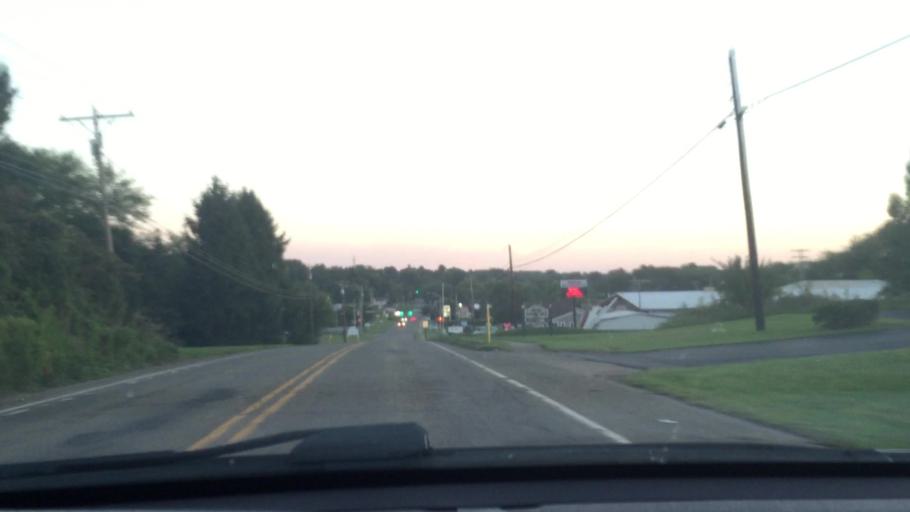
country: US
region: Pennsylvania
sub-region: Butler County
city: Slippery Rock
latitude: 41.0738
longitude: -80.0517
